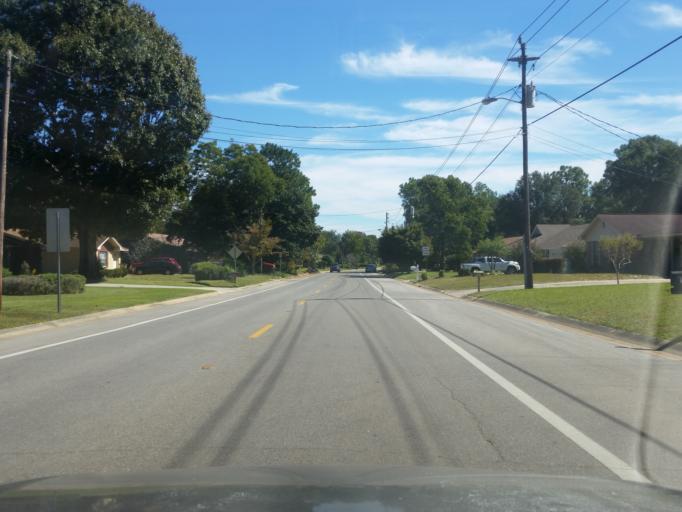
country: US
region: Florida
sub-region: Escambia County
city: East Pensacola Heights
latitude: 30.4621
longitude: -87.1738
